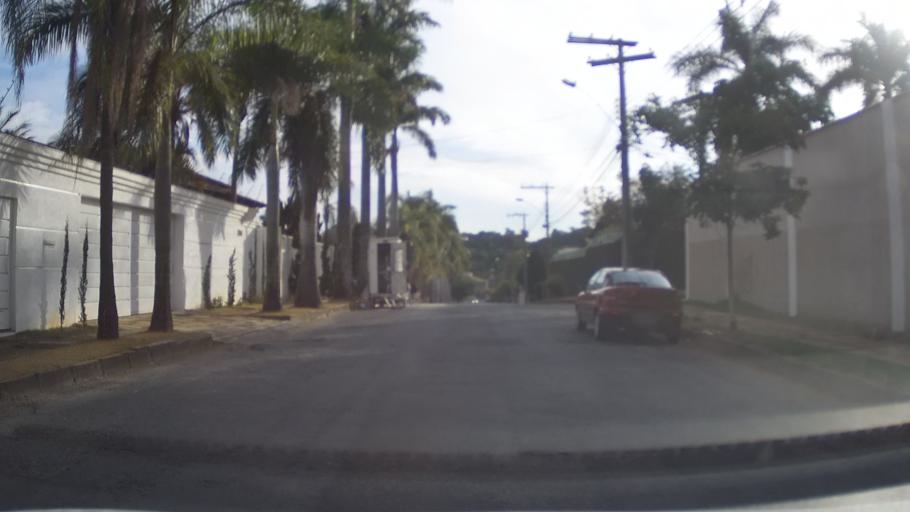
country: BR
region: Minas Gerais
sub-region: Belo Horizonte
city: Belo Horizonte
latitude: -19.8620
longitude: -43.9956
